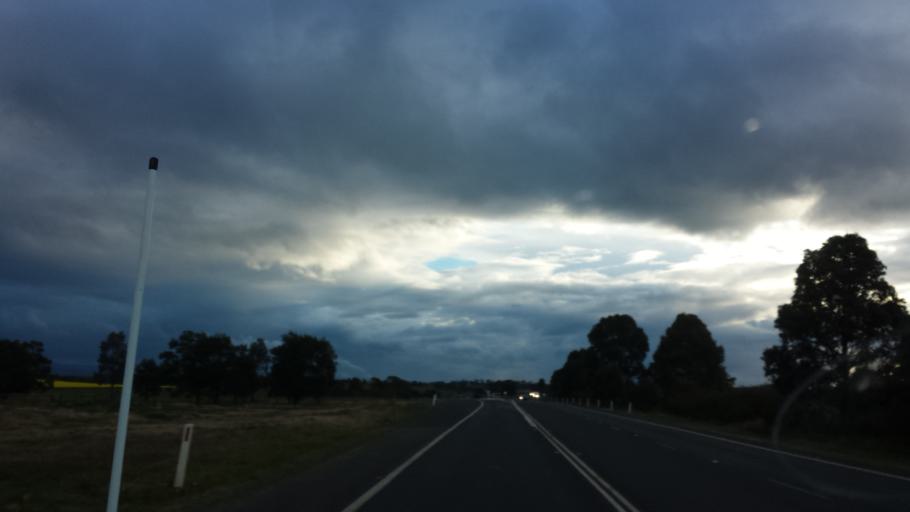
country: AU
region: Victoria
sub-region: Wellington
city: Heyfield
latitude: -38.1276
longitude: 146.8346
